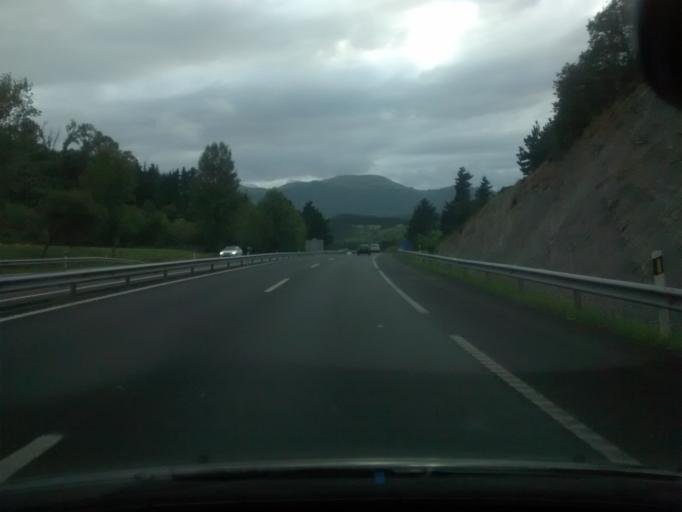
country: ES
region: Basque Country
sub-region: Provincia de Guipuzcoa
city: Zumaia
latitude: 43.2717
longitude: -2.2603
